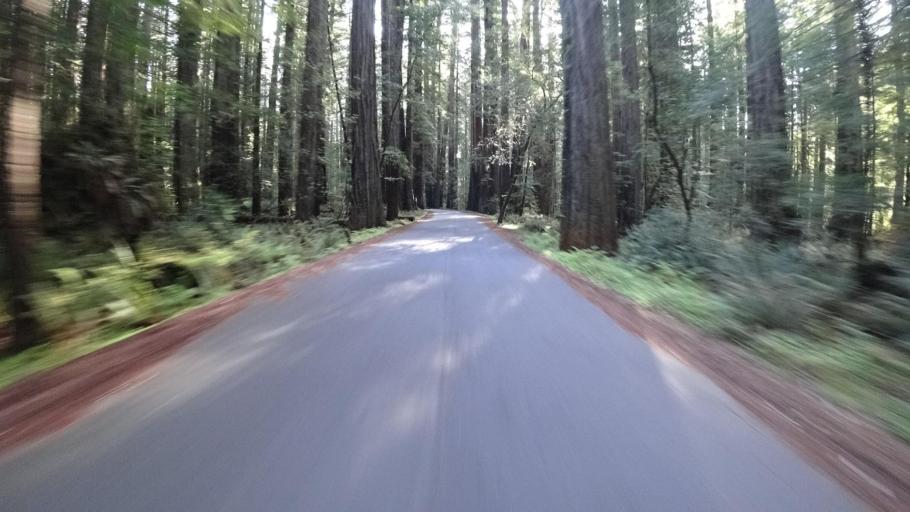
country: US
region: California
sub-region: Humboldt County
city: Rio Dell
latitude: 40.3514
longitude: -123.9960
